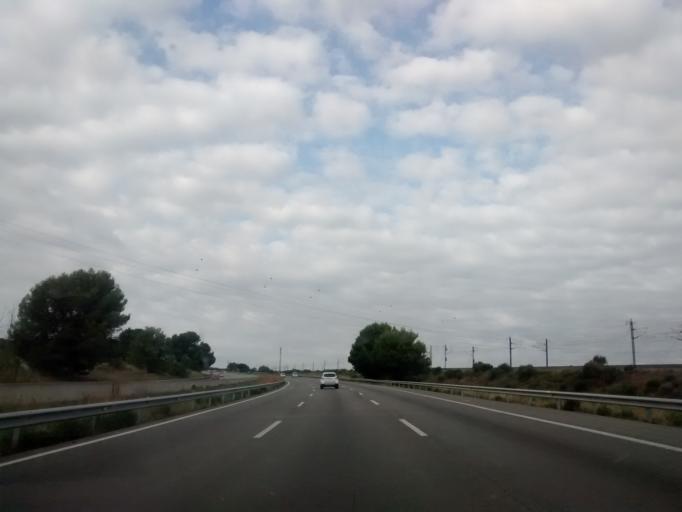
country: ES
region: Catalonia
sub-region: Provincia de Barcelona
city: La Granada
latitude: 41.3848
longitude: 1.7427
